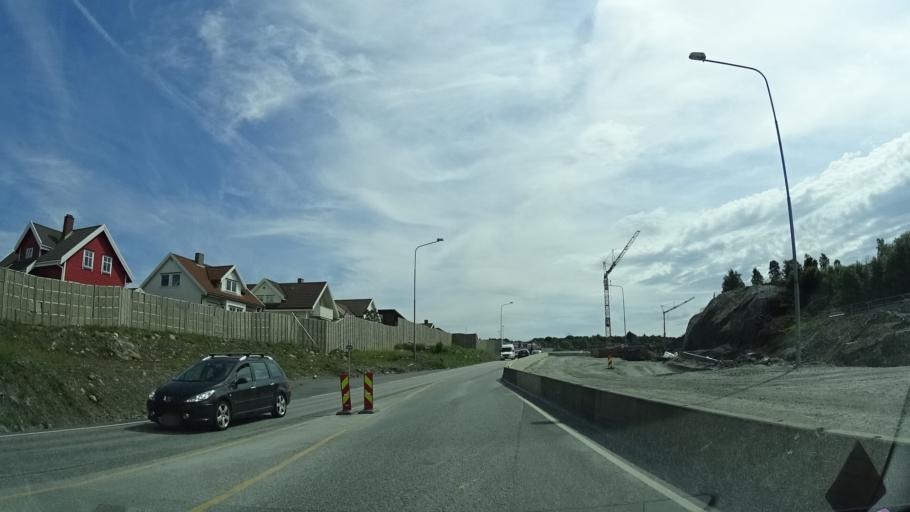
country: NO
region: Rogaland
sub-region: Stavanger
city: Stavanger
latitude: 58.9800
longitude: 5.6840
